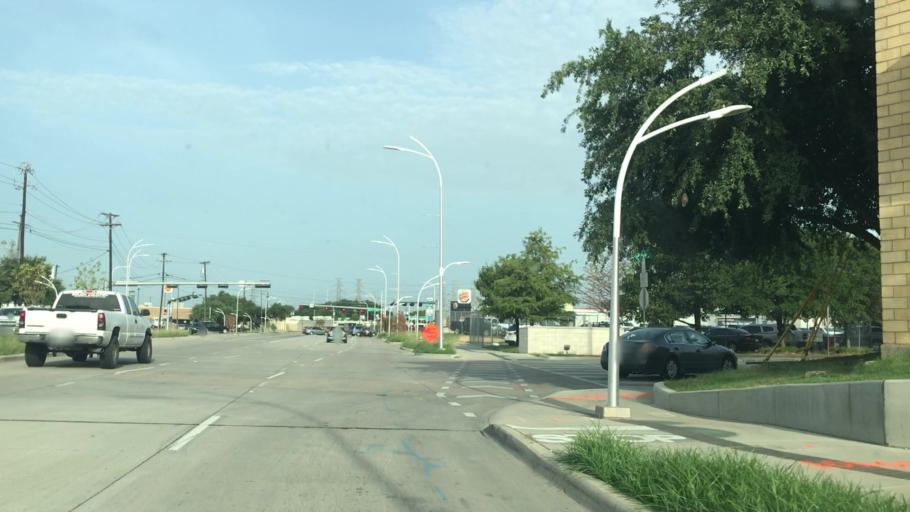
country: US
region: Texas
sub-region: Dallas County
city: Dallas
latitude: 32.7839
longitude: -96.8140
